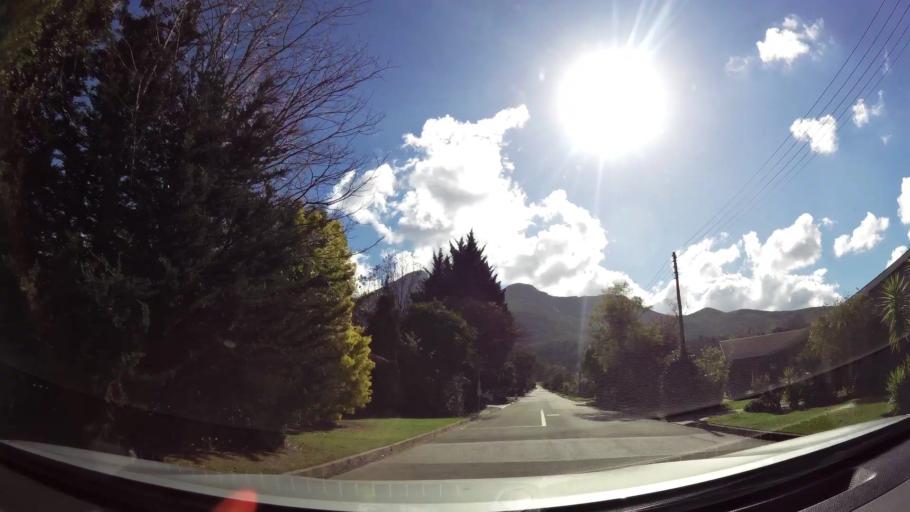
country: ZA
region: Western Cape
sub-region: Eden District Municipality
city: George
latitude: -33.9419
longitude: 22.4760
